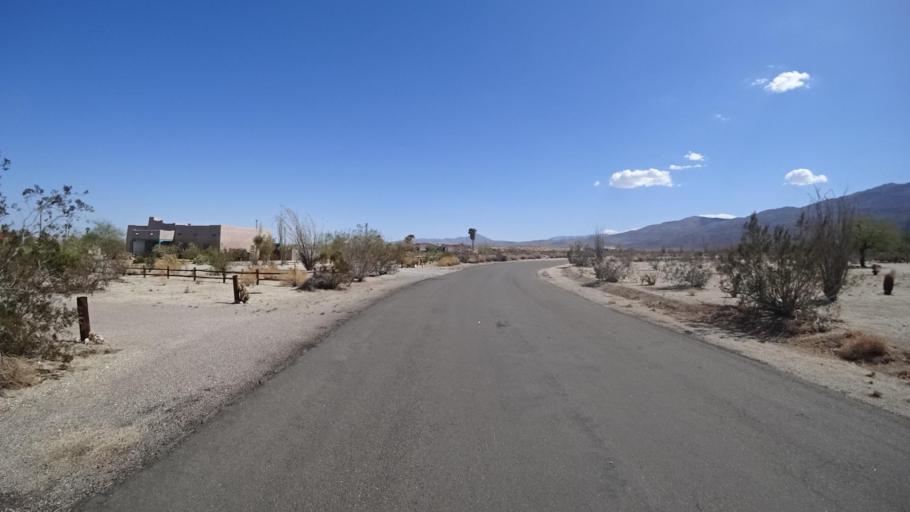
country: US
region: California
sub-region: San Diego County
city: Borrego Springs
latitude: 33.2280
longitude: -116.3877
